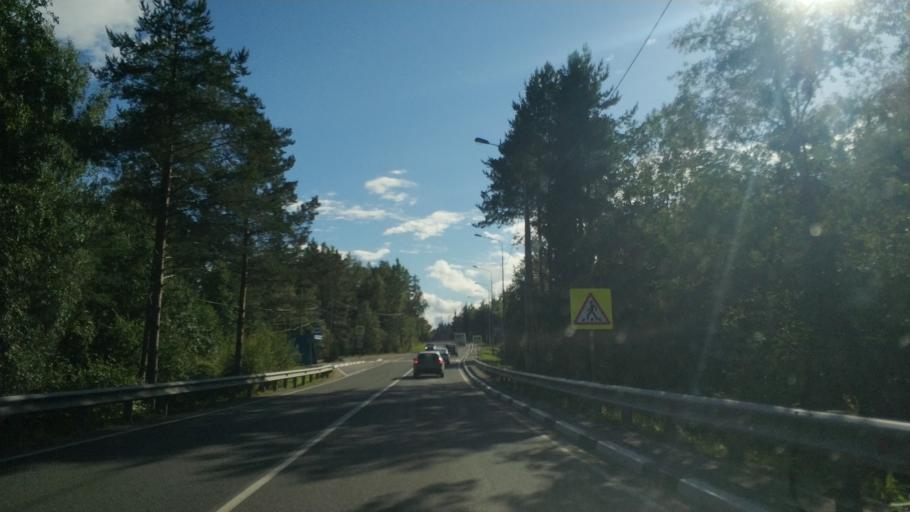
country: RU
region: Republic of Karelia
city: Lakhdenpokh'ya
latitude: 61.5304
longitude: 30.2061
